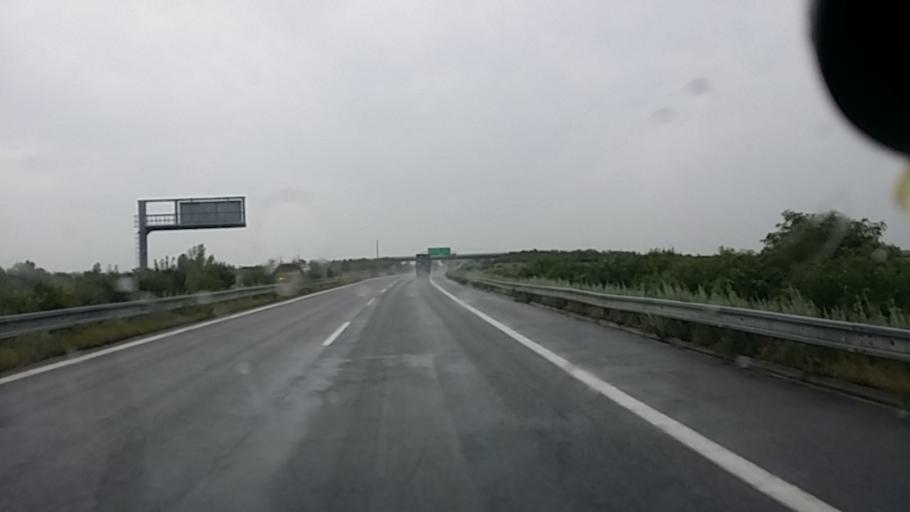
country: HU
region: Gyor-Moson-Sopron
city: Rajka
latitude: 48.0231
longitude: 17.1664
